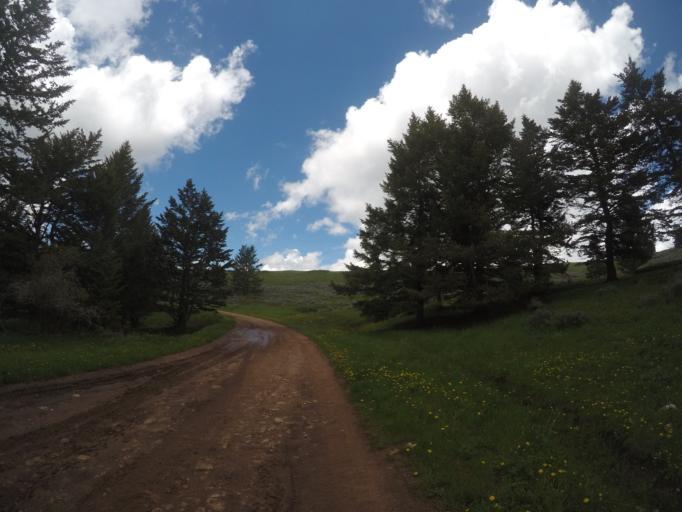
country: US
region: Wyoming
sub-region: Big Horn County
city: Lovell
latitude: 45.1755
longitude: -108.4340
